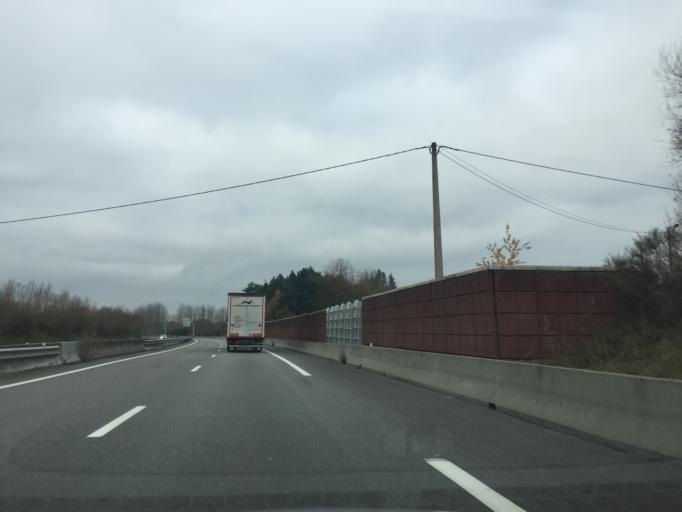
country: FR
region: Limousin
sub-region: Departement de la Creuse
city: Gouzon
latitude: 46.1989
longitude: 2.2471
